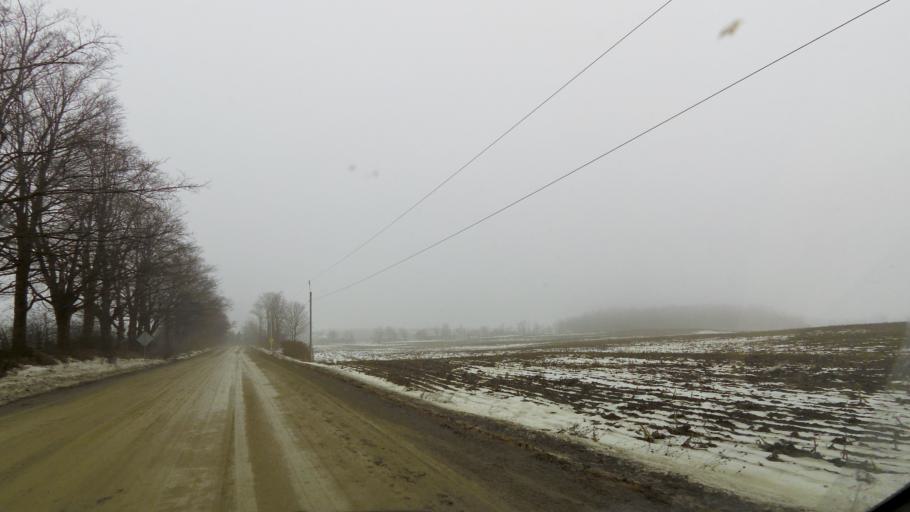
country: CA
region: Ontario
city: Brampton
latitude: 43.8401
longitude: -79.8546
